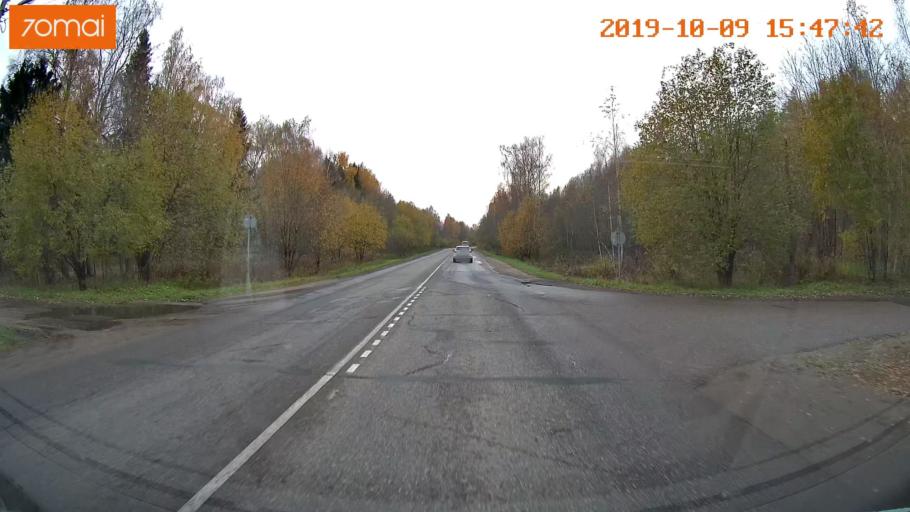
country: RU
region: Kostroma
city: Oktyabr'skiy
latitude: 57.8158
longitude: 41.0251
